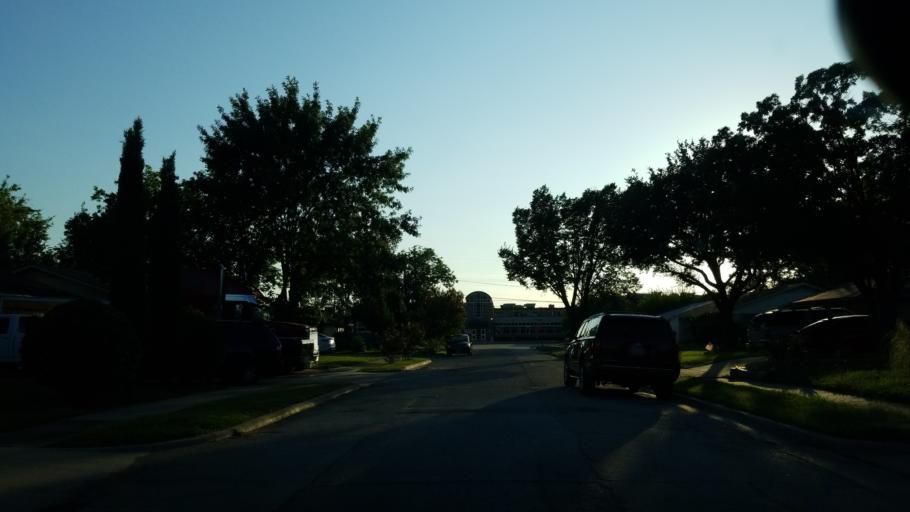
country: US
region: Texas
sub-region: Dallas County
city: Carrollton
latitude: 32.9485
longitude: -96.8892
